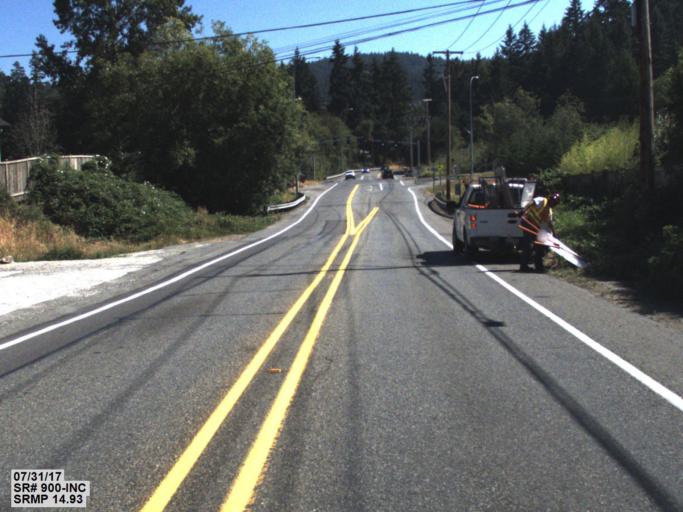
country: US
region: Washington
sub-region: King County
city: Newcastle
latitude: 47.5046
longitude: -122.1454
